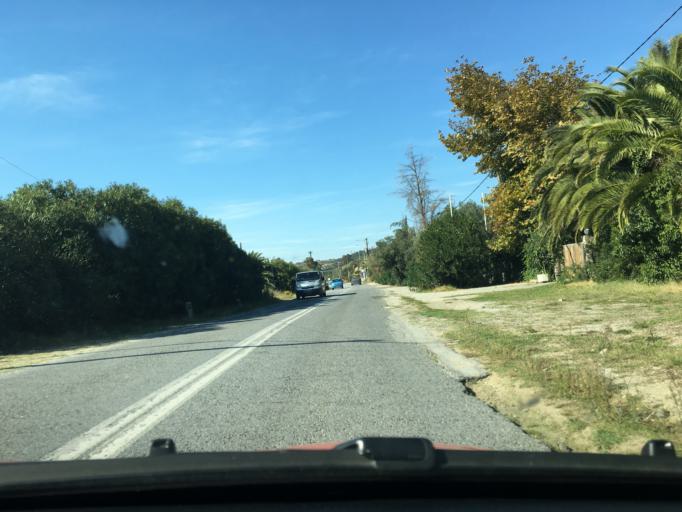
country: GR
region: Central Macedonia
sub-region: Nomos Chalkidikis
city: Ouranoupolis
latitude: 40.3423
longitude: 23.9687
